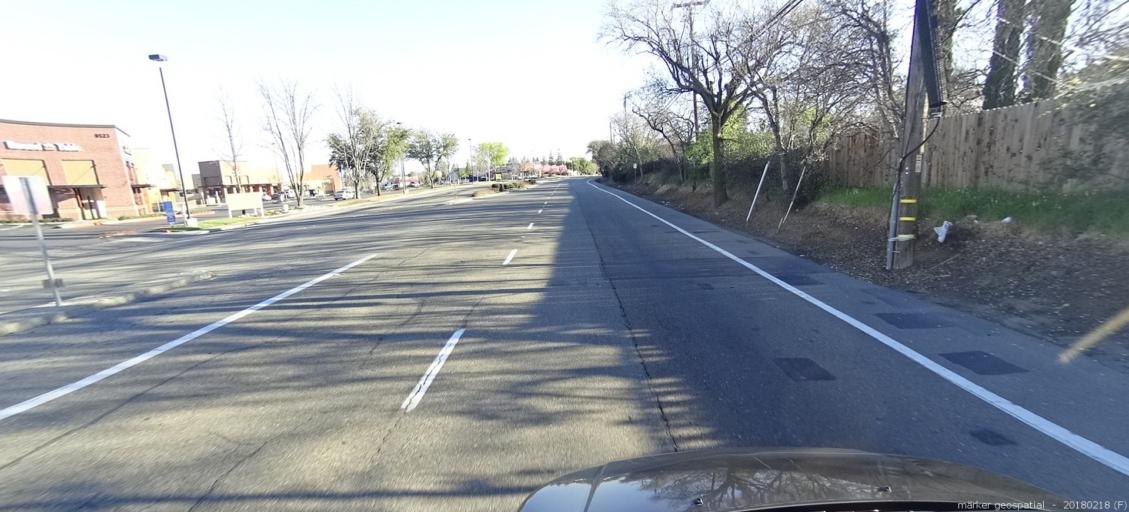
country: US
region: California
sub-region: Sacramento County
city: Folsom
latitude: 38.6748
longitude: -121.1996
